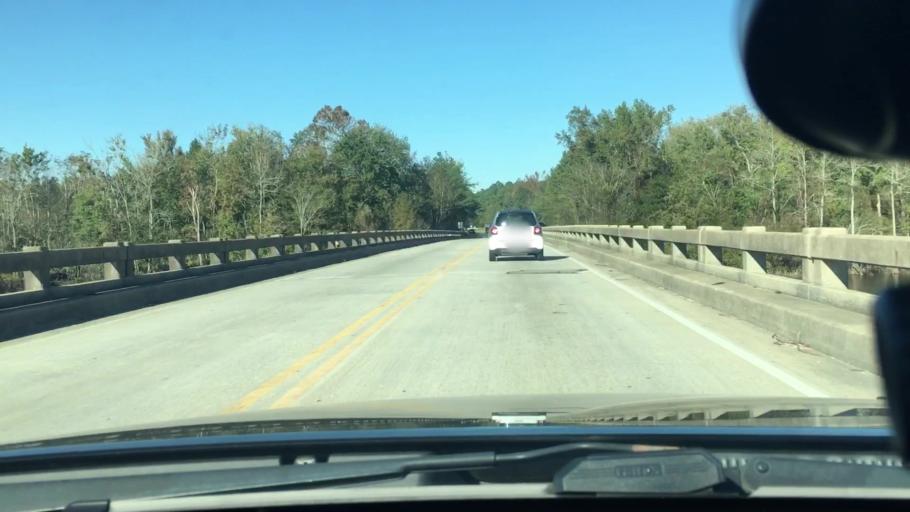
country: US
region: North Carolina
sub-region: Craven County
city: Vanceboro
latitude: 35.2107
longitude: -77.1227
